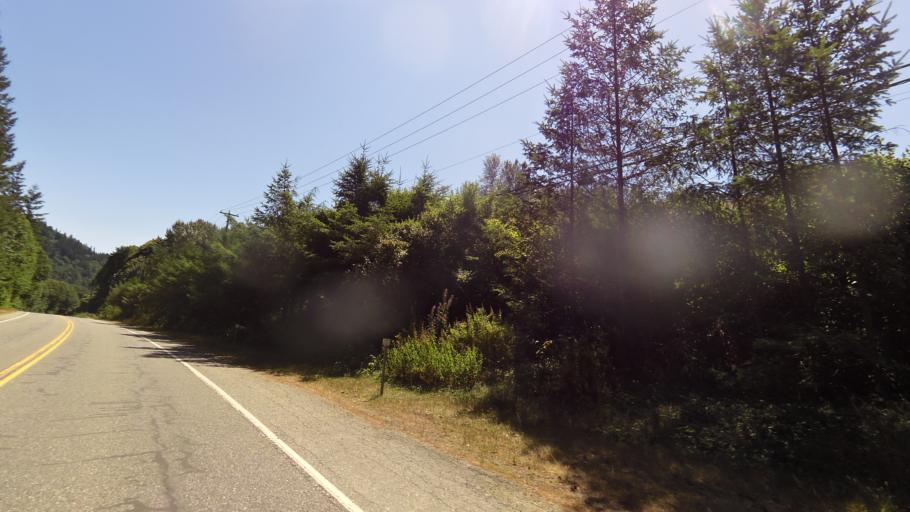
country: CA
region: British Columbia
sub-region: Fraser Valley Regional District
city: Chilliwack
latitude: 49.2257
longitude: -122.0156
